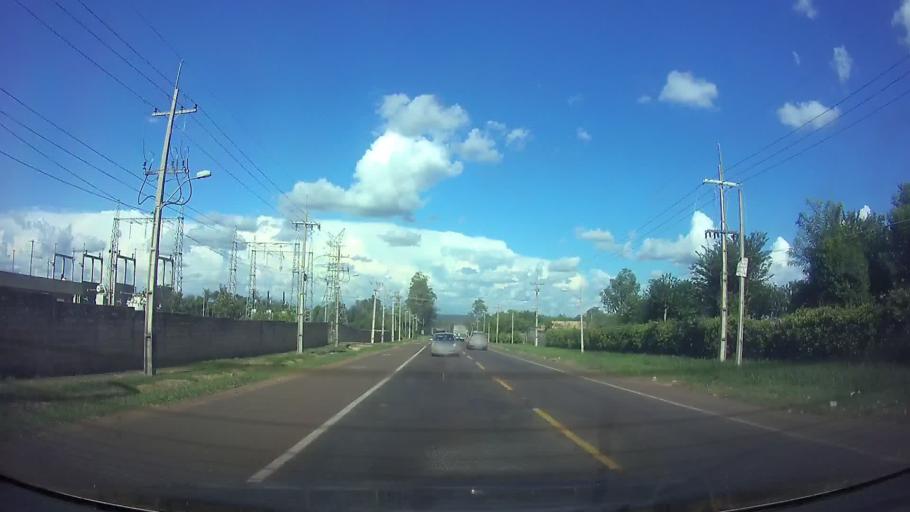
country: PY
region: Cordillera
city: Eusebio Ayala
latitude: -25.3815
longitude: -56.9997
